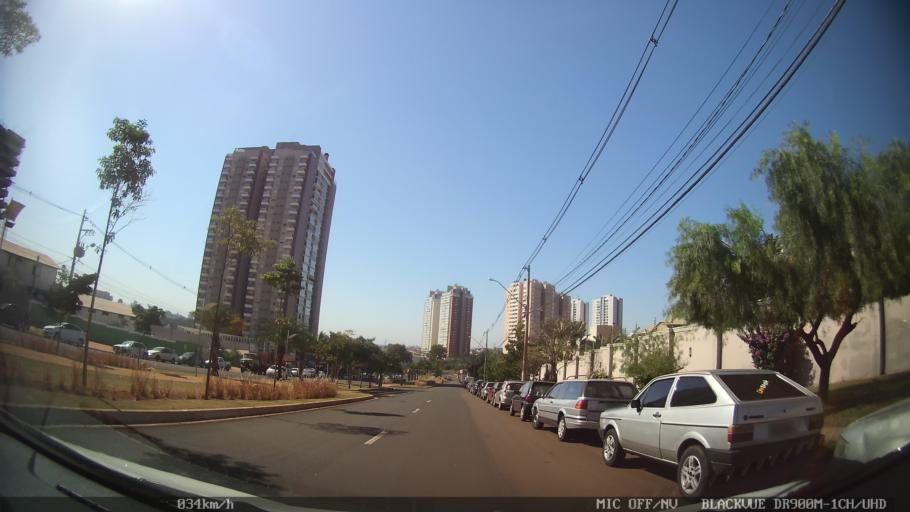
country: BR
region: Sao Paulo
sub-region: Ribeirao Preto
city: Ribeirao Preto
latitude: -21.2195
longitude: -47.7998
